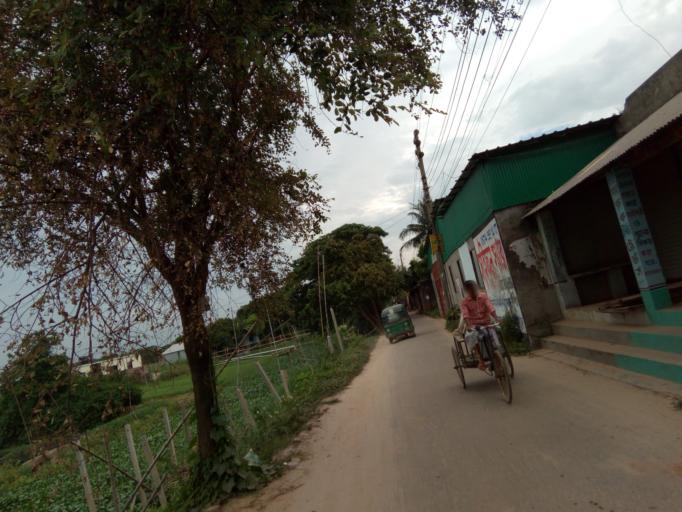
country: BD
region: Dhaka
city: Paltan
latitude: 23.7582
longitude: 90.4599
